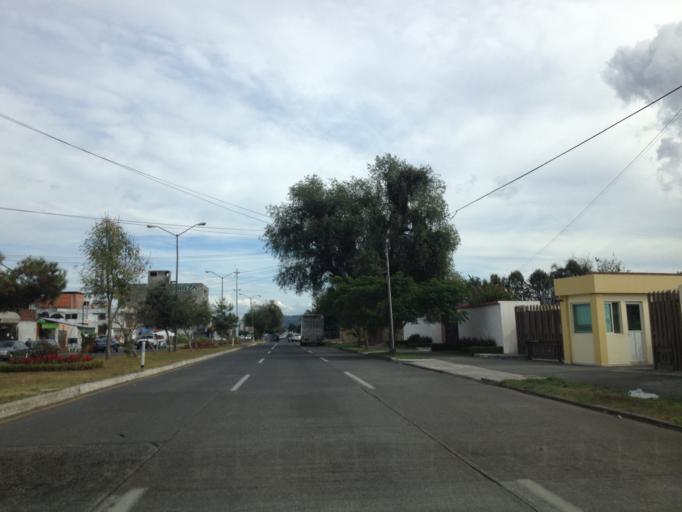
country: MX
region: Michoacan
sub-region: Uruapan
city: Uruapan
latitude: 19.4040
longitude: -102.0466
